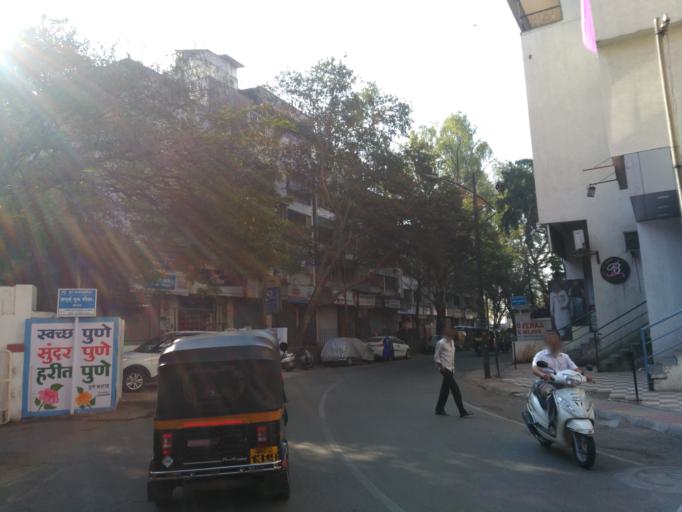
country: IN
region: Maharashtra
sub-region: Pune Division
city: Pune
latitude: 18.5103
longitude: 73.8724
